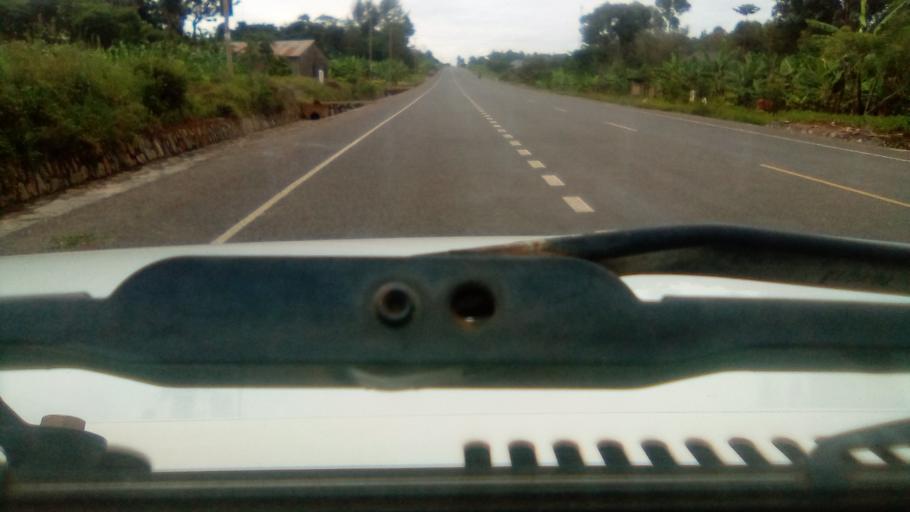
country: UG
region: Eastern Region
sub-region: Mbale District
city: Mbale
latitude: 0.9854
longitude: 34.1855
